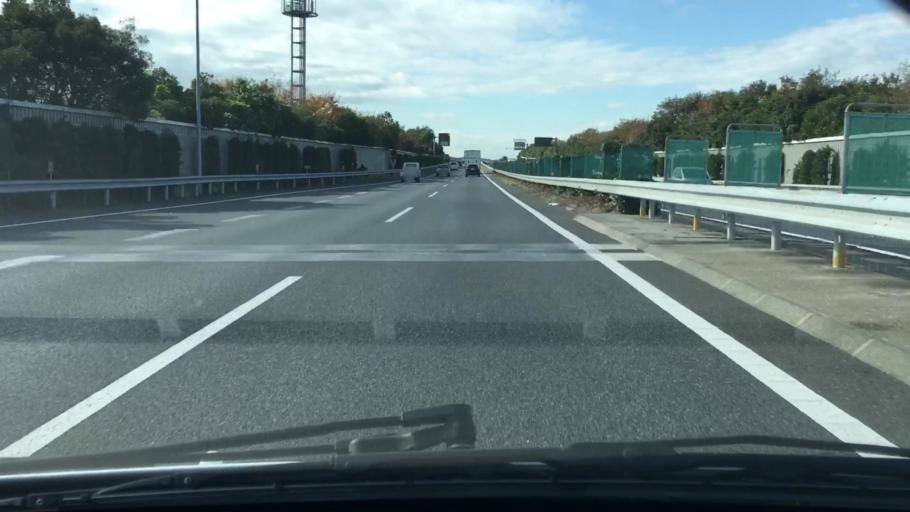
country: JP
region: Chiba
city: Ichihara
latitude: 35.4938
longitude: 140.0910
